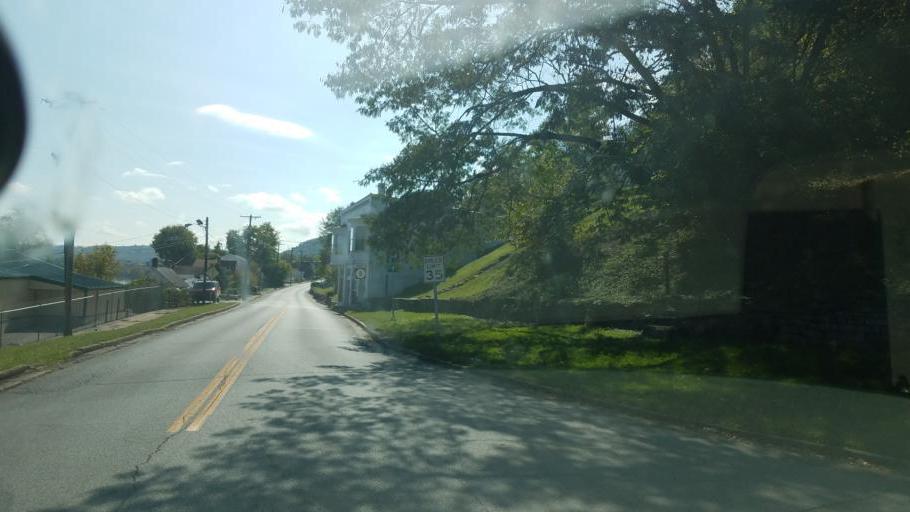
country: US
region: Ohio
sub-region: Brown County
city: Aberdeen
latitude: 38.6576
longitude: -83.7770
